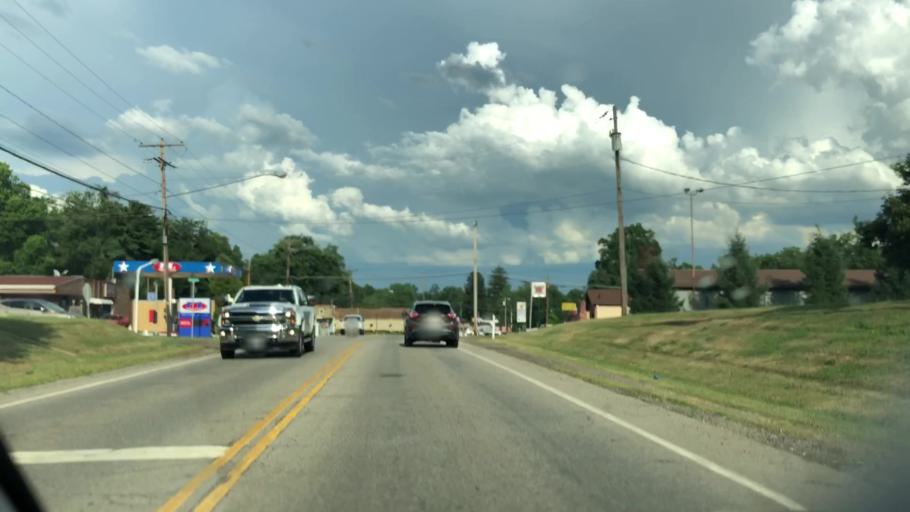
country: US
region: Ohio
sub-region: Summit County
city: Portage Lakes
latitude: 40.9811
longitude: -81.5380
